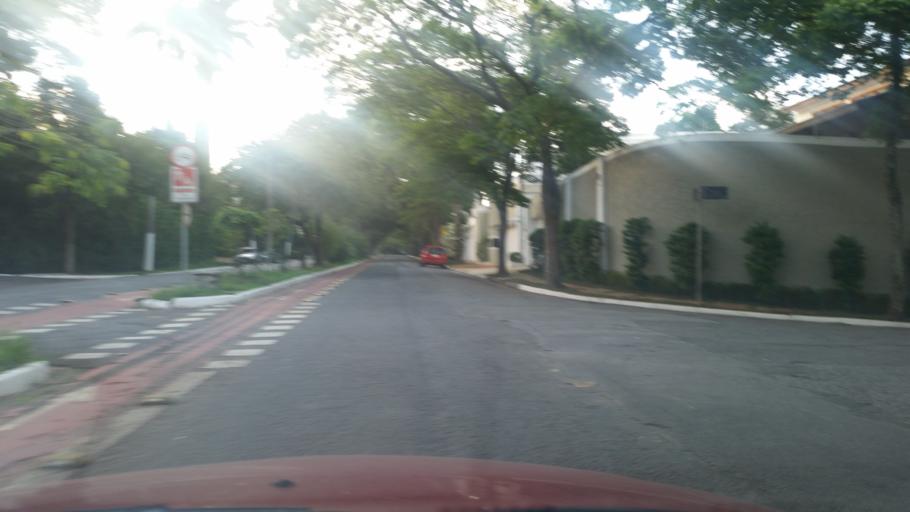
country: BR
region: Sao Paulo
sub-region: Diadema
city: Diadema
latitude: -23.6379
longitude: -46.6821
